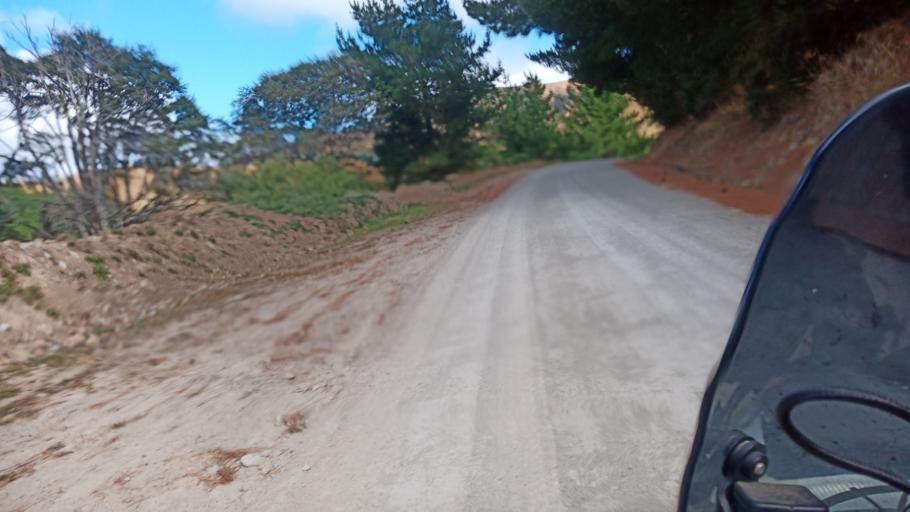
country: NZ
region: Hawke's Bay
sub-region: Wairoa District
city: Wairoa
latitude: -38.6048
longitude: 177.4885
